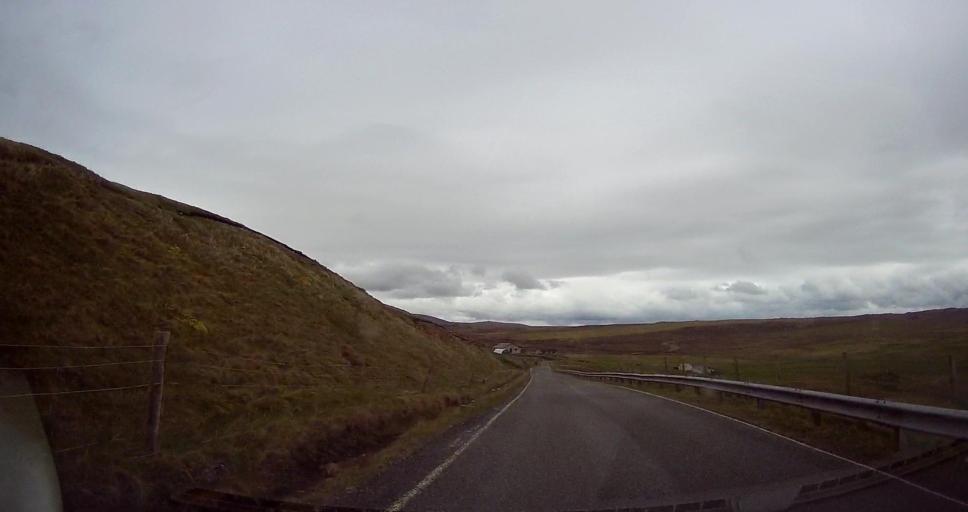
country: GB
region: Scotland
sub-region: Shetland Islands
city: Lerwick
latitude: 60.4863
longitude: -1.4990
